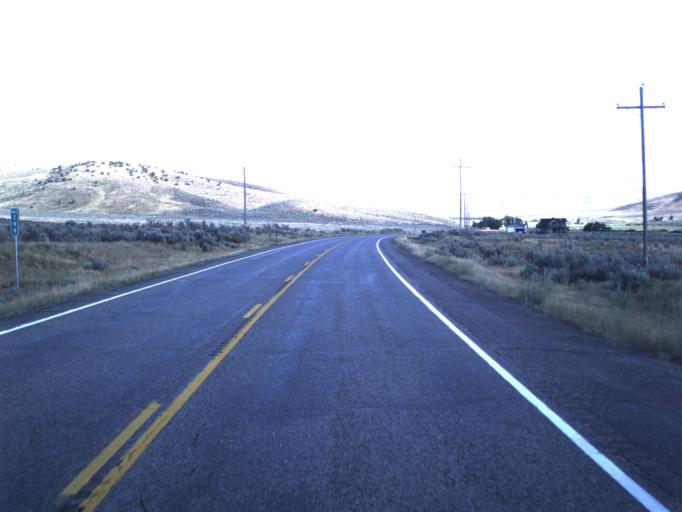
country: US
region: Utah
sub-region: Utah County
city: Woodland Hills
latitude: 39.8404
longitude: -111.5137
